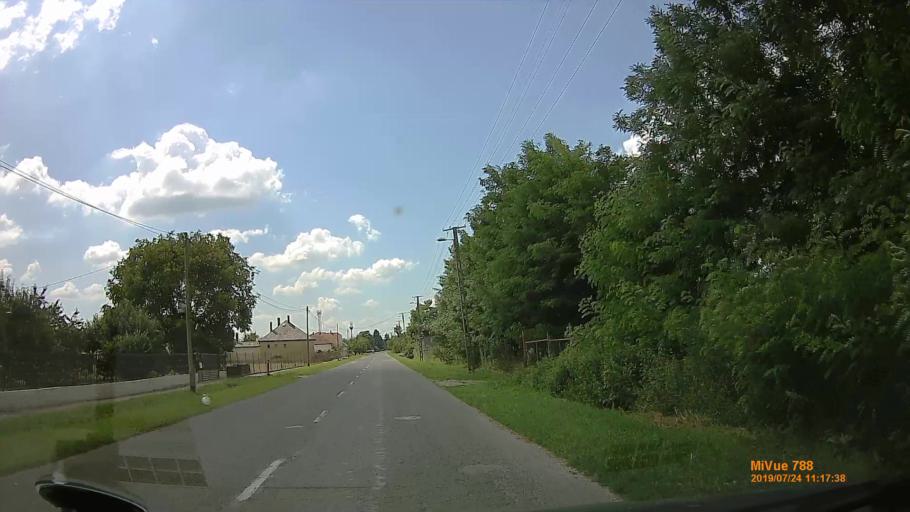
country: HU
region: Szabolcs-Szatmar-Bereg
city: Tarpa
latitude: 48.1683
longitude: 22.4598
